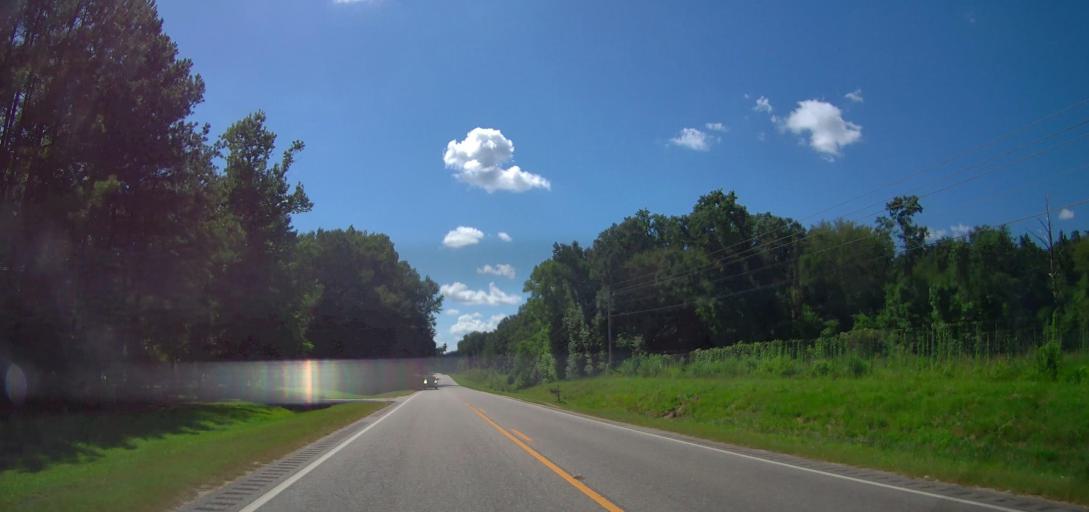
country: US
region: Alabama
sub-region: Macon County
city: Tuskegee
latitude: 32.3822
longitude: -85.8037
